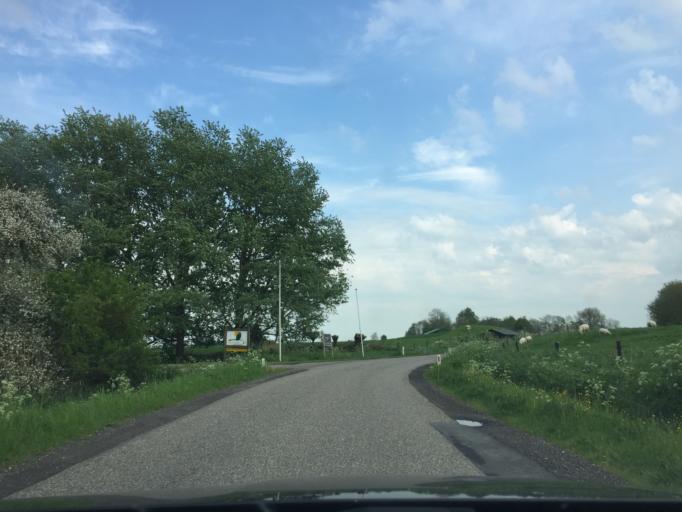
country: NL
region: Groningen
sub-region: Gemeente Zuidhorn
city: Oldehove
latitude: 53.3127
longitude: 6.3614
